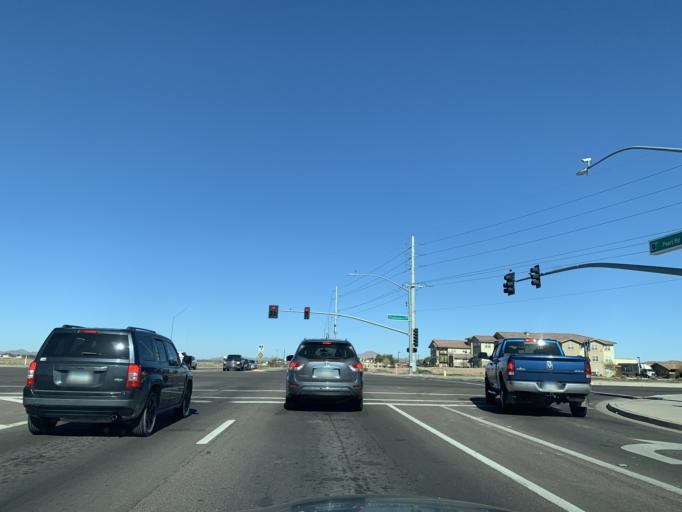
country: US
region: Arizona
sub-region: Pinal County
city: Casa Grande
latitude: 32.8939
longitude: -111.7226
